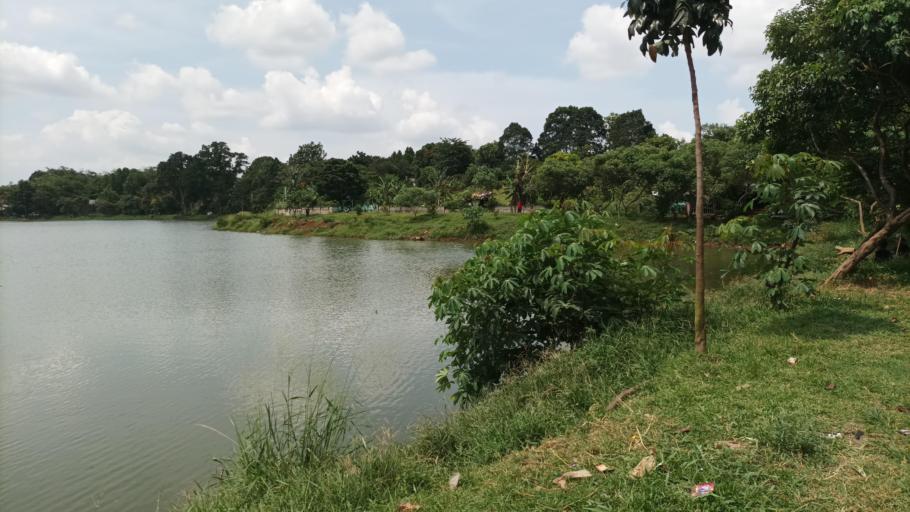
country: ID
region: West Java
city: Cibinong
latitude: -6.4503
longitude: 106.8602
